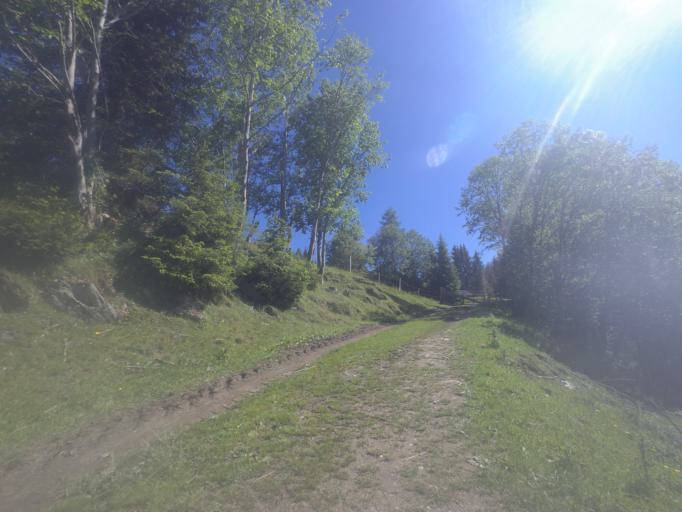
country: AT
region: Salzburg
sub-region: Politischer Bezirk Zell am See
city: Lend
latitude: 47.3237
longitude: 13.0431
